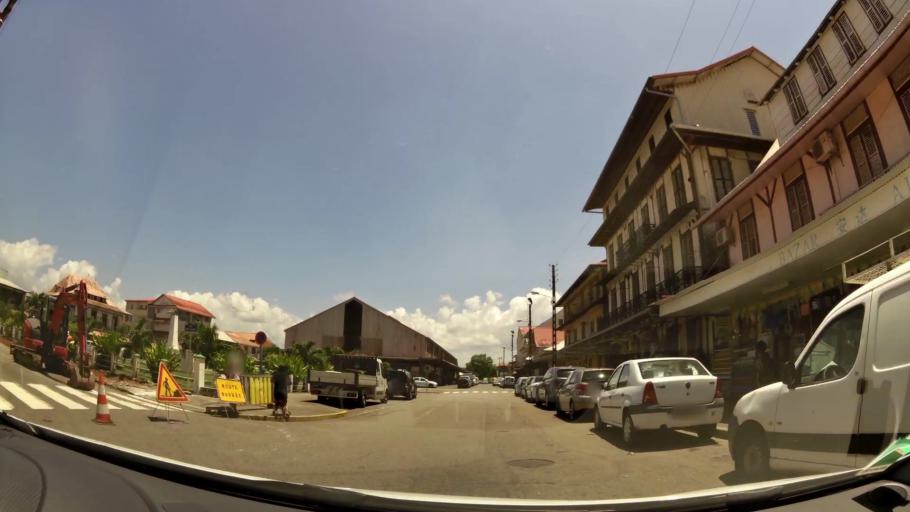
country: GF
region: Guyane
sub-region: Guyane
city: Cayenne
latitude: 4.9365
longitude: -52.3343
